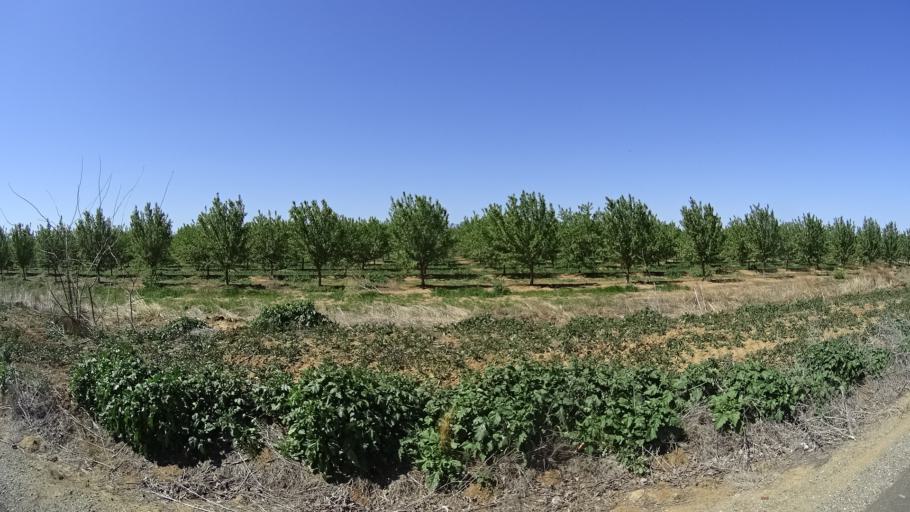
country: US
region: California
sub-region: Glenn County
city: Willows
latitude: 39.5046
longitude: -122.2492
